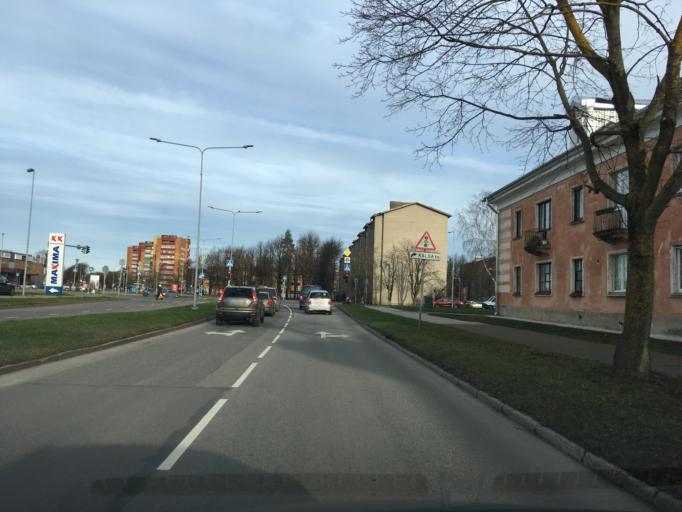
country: EE
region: Ida-Virumaa
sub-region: Narva linn
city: Narva
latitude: 59.3641
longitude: 28.1882
